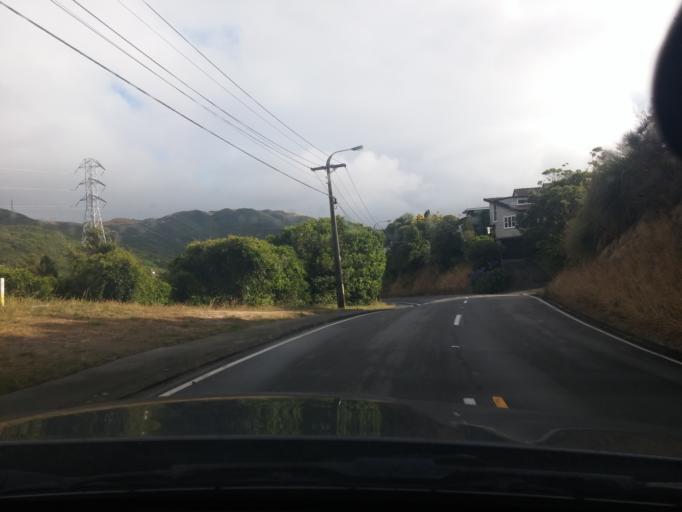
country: NZ
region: Wellington
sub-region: Wellington City
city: Kelburn
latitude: -41.2734
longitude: 174.7551
